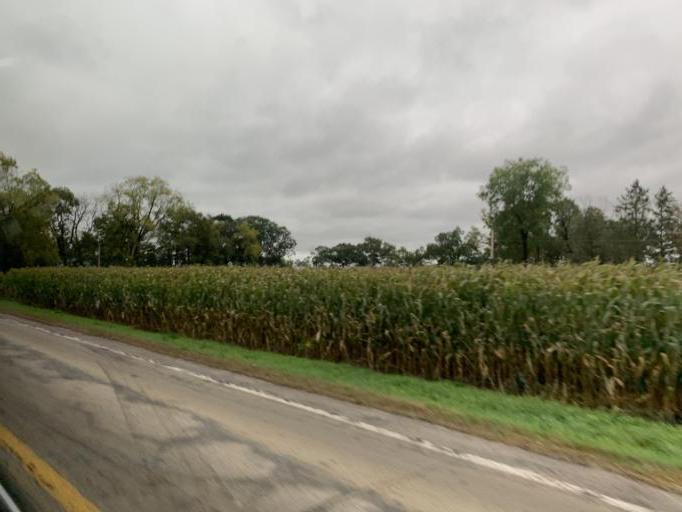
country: US
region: Wisconsin
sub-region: Grant County
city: Muscoda
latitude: 43.2051
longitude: -90.3937
